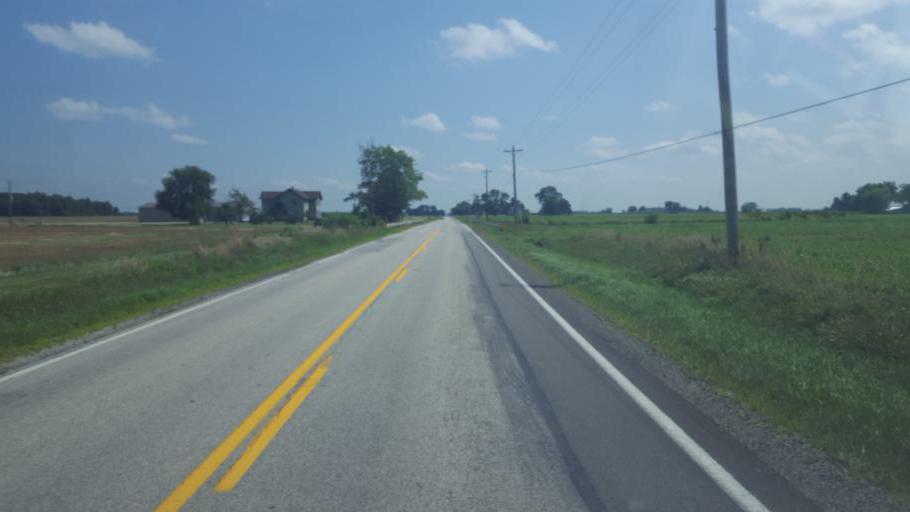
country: US
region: Ohio
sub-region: Huron County
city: Bellevue
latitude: 41.2397
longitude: -82.8396
